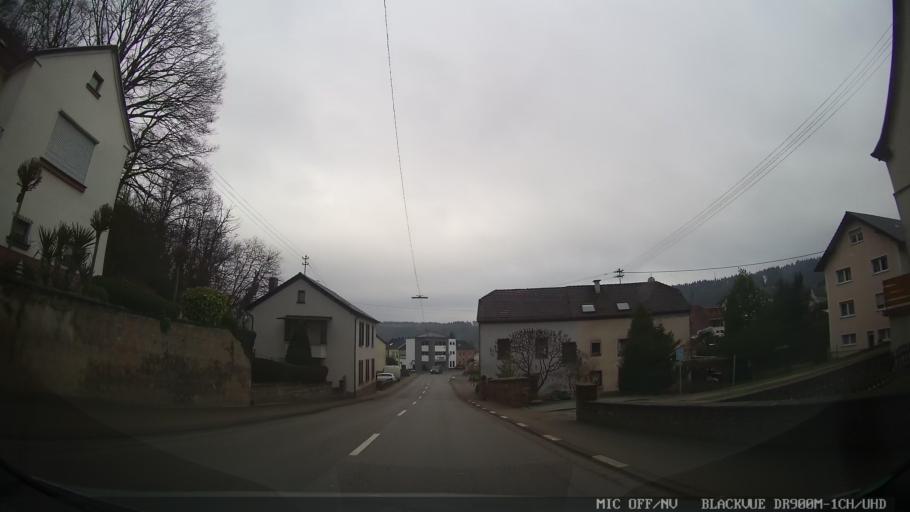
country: DE
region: Saarland
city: Mettlach
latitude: 49.4991
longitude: 6.5849
